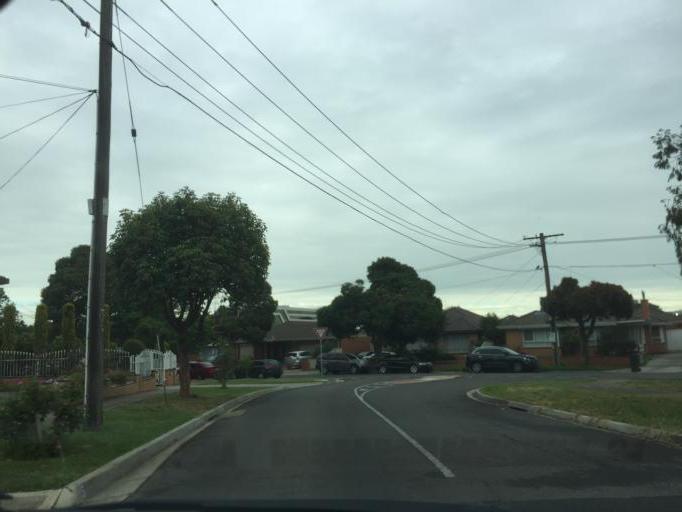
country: AU
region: Victoria
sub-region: Brimbank
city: Sunshine North
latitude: -37.7844
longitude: 144.8375
